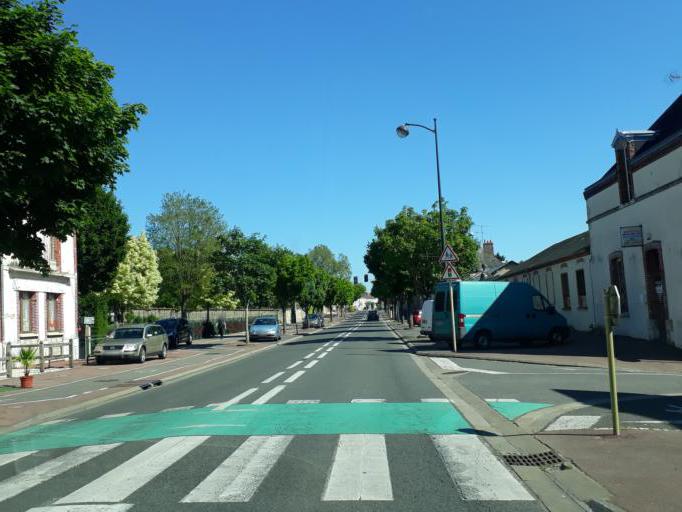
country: FR
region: Centre
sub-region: Departement du Loiret
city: Briare
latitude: 47.6456
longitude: 2.7319
